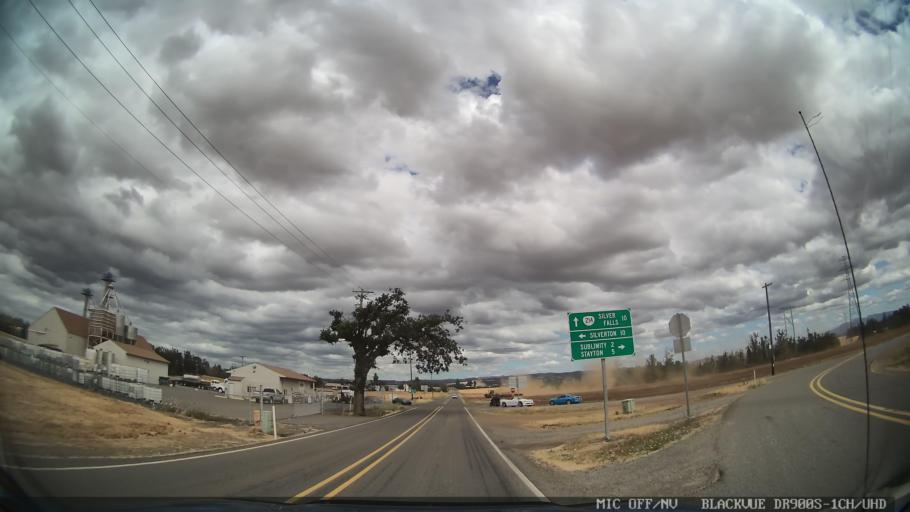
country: US
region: Oregon
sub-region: Marion County
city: Sublimity
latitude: 44.8662
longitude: -122.7926
